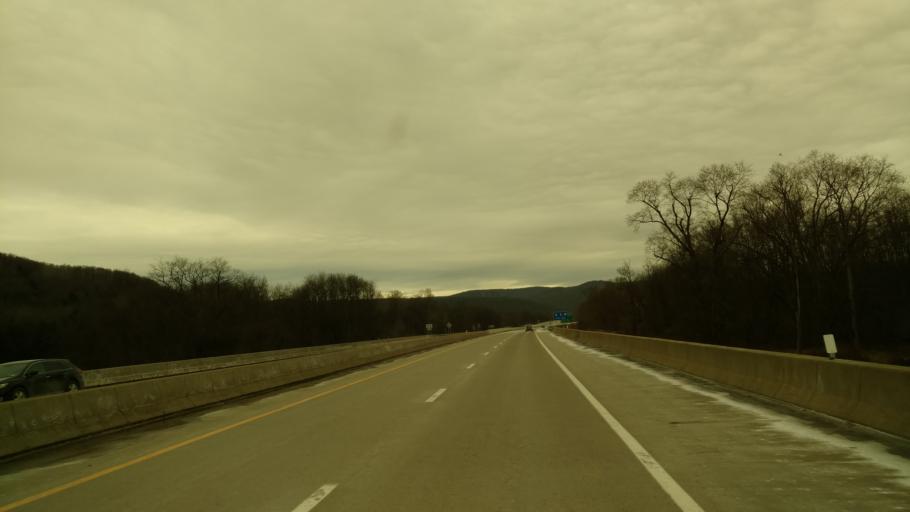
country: US
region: Pennsylvania
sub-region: McKean County
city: Foster Brook
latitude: 42.0864
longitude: -78.6189
